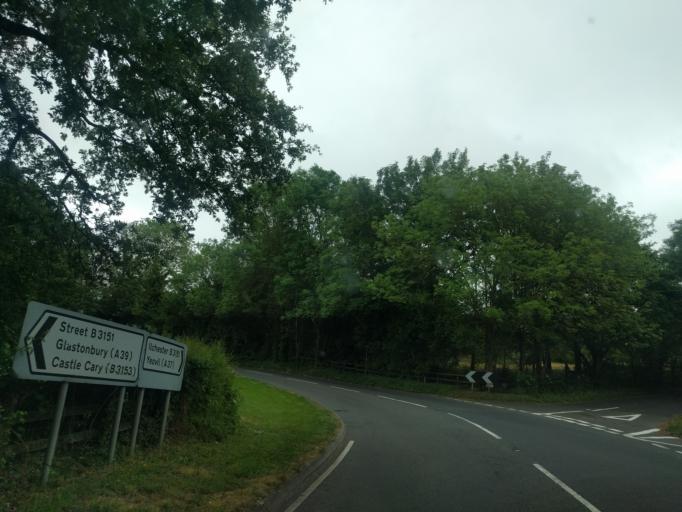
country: GB
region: England
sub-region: Somerset
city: Ilchester
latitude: 51.0560
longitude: -2.7212
